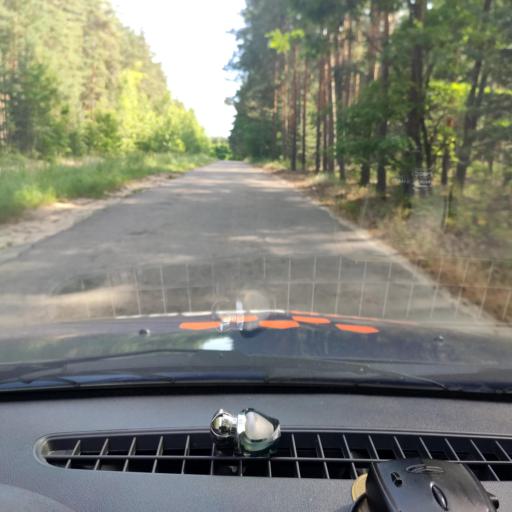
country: RU
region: Voronezj
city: Somovo
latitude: 51.7717
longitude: 39.3673
